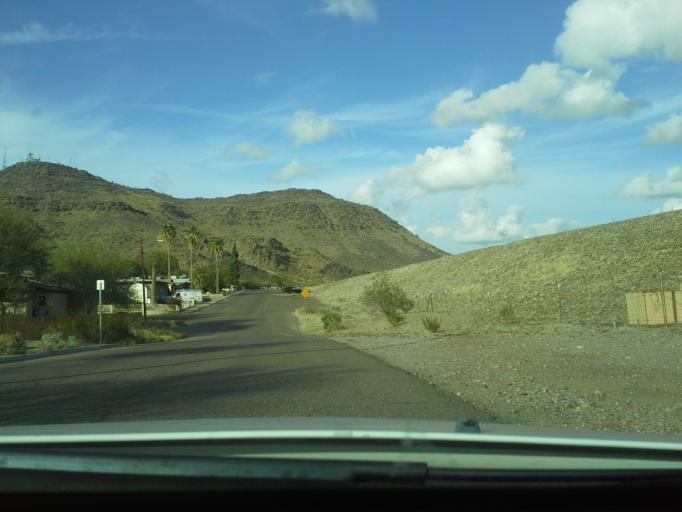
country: US
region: Arizona
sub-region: Maricopa County
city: Glendale
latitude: 33.5833
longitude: -112.0823
